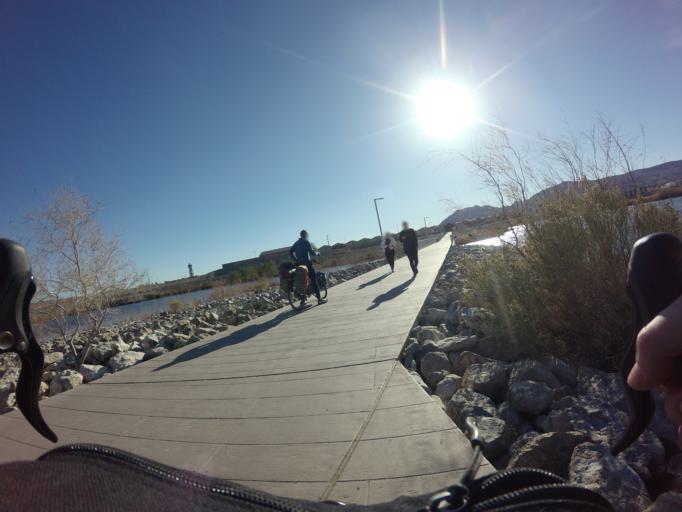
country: US
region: Nevada
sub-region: Clark County
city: Whitney
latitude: 36.0395
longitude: -115.0528
